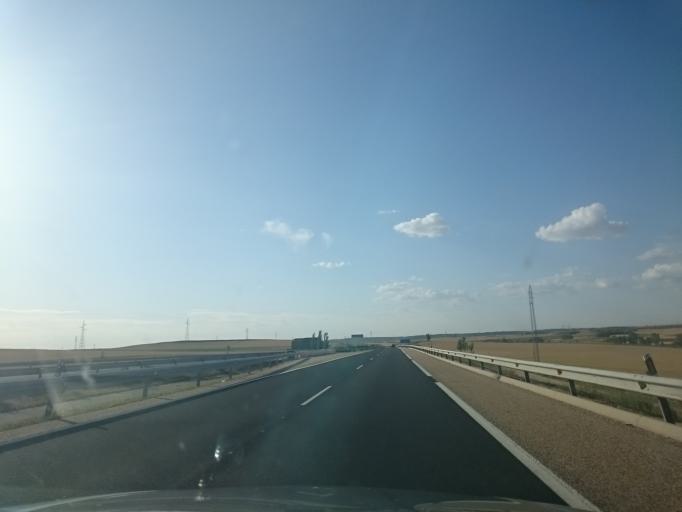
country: ES
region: Castille and Leon
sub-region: Provincia de Burgos
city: Villagonzalo-Pedernales
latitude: 42.3168
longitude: -3.7627
